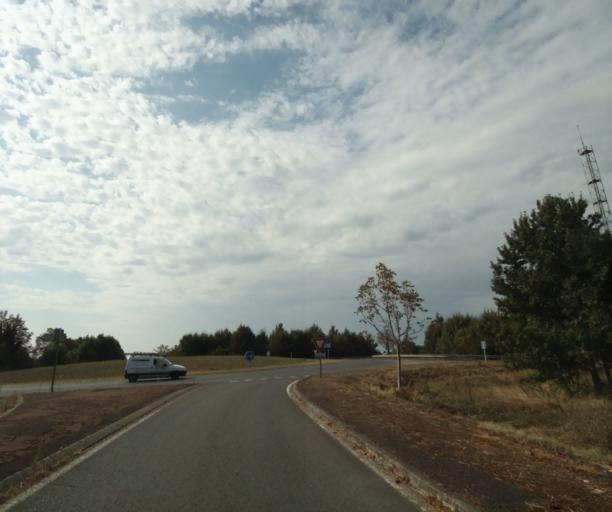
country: FR
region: Poitou-Charentes
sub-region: Departement de la Charente-Maritime
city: Cabariot
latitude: 45.9576
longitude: -0.8593
